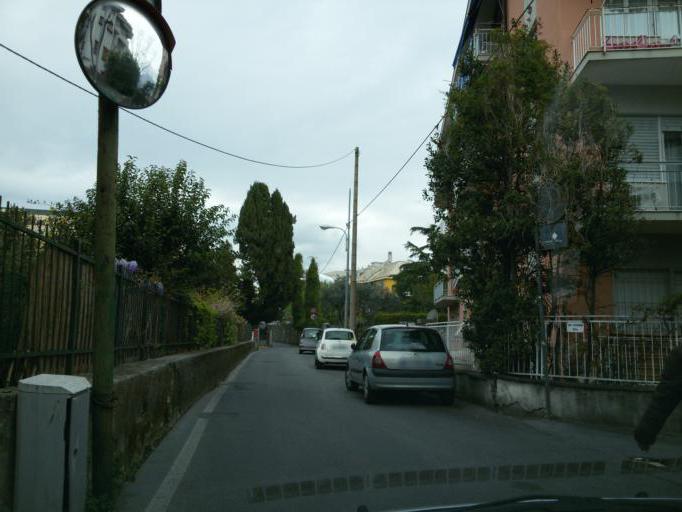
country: IT
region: Liguria
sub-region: Provincia di Genova
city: Genoa
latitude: 44.4017
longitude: 8.9749
